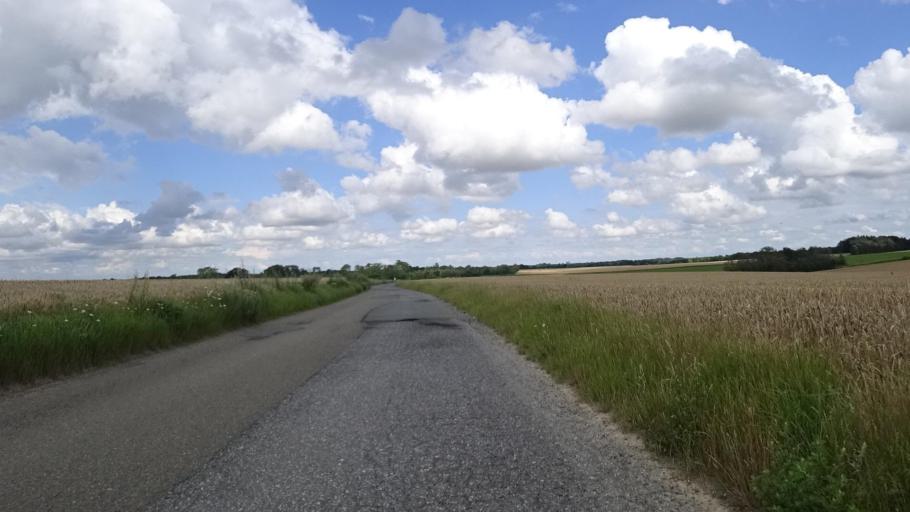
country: BE
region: Wallonia
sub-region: Province du Brabant Wallon
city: Villers-la-Ville
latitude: 50.5545
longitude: 4.5178
